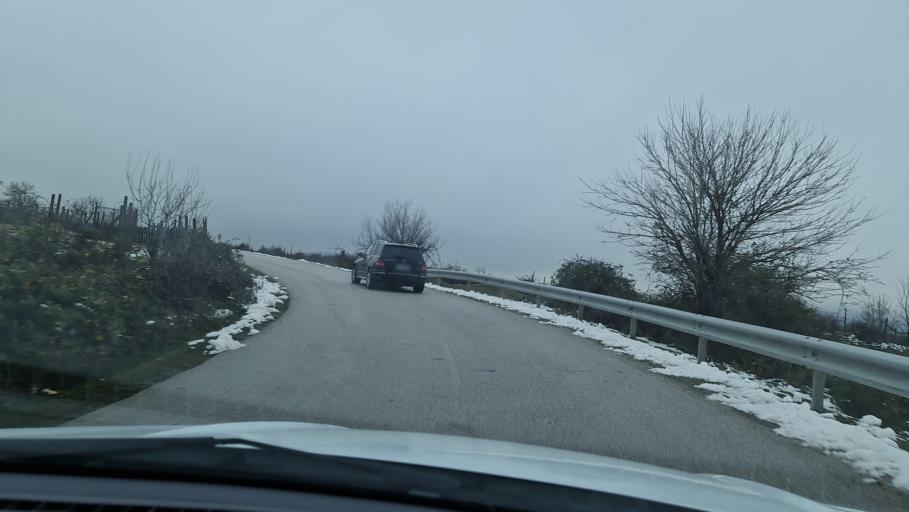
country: AL
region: Kukes
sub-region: Rrethi i Kukesit
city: Kolsh
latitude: 42.0718
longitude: 20.3262
